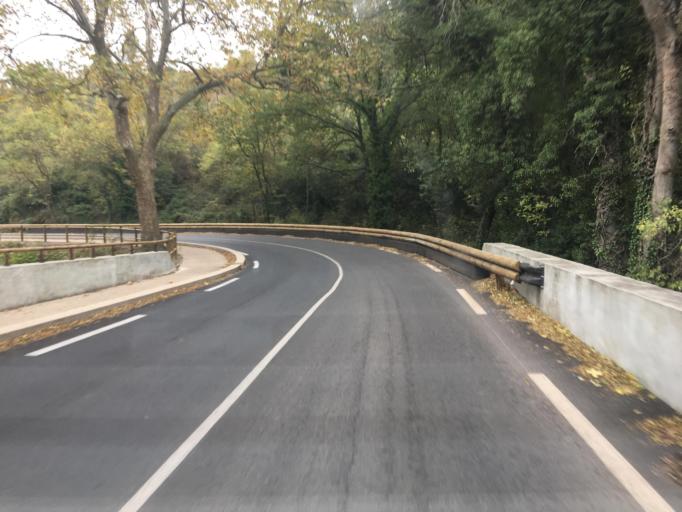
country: FR
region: Languedoc-Roussillon
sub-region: Departement de l'Herault
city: Nebian
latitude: 43.6402
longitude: 3.4132
